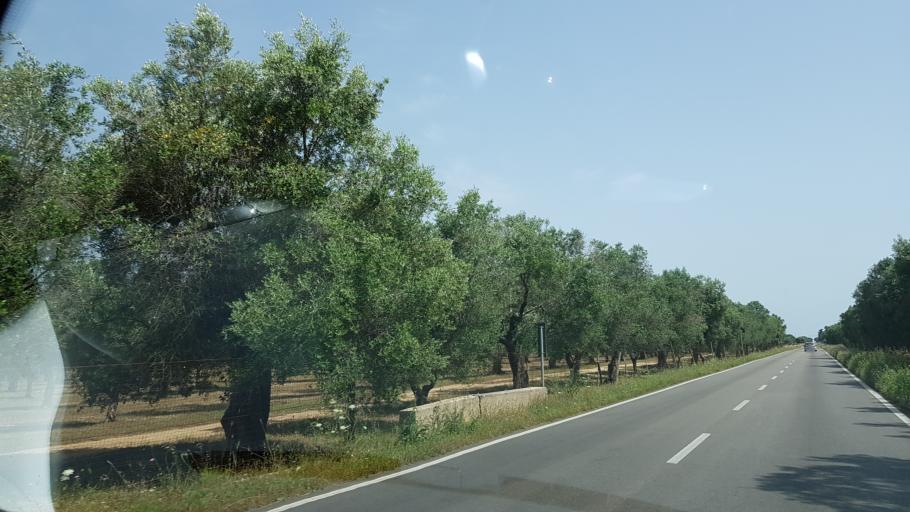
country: IT
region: Apulia
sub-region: Provincia di Brindisi
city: San Pancrazio Salentino
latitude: 40.3596
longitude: 17.8430
